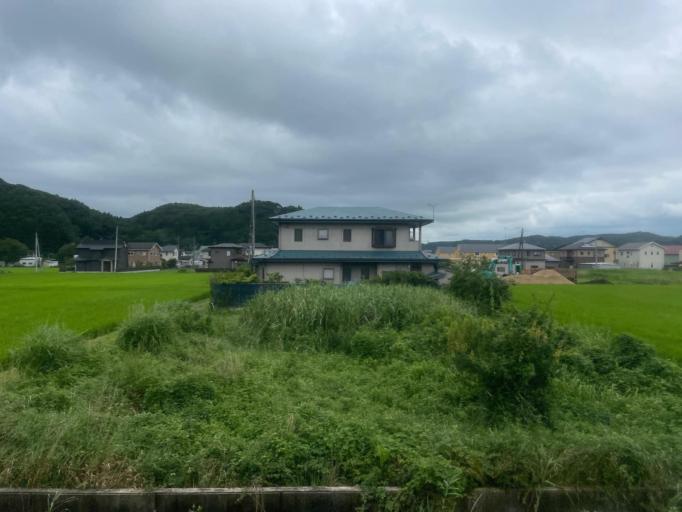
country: JP
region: Fukushima
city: Ishikawa
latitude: 37.1308
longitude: 140.2487
